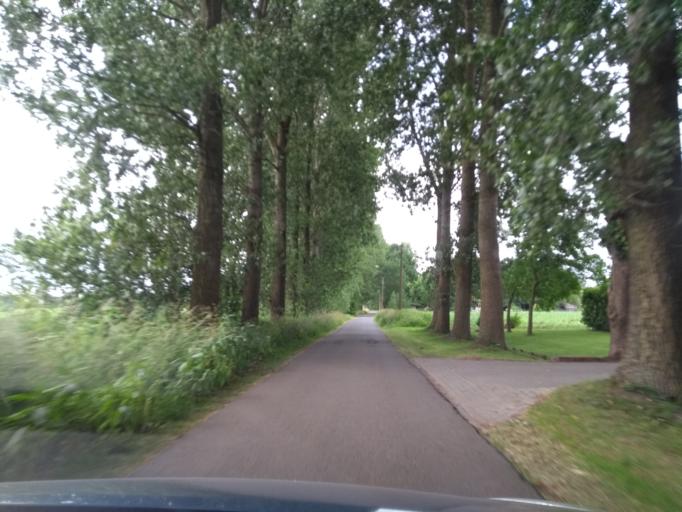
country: BE
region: Flanders
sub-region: Provincie Oost-Vlaanderen
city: Nevele
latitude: 51.0738
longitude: 3.5174
